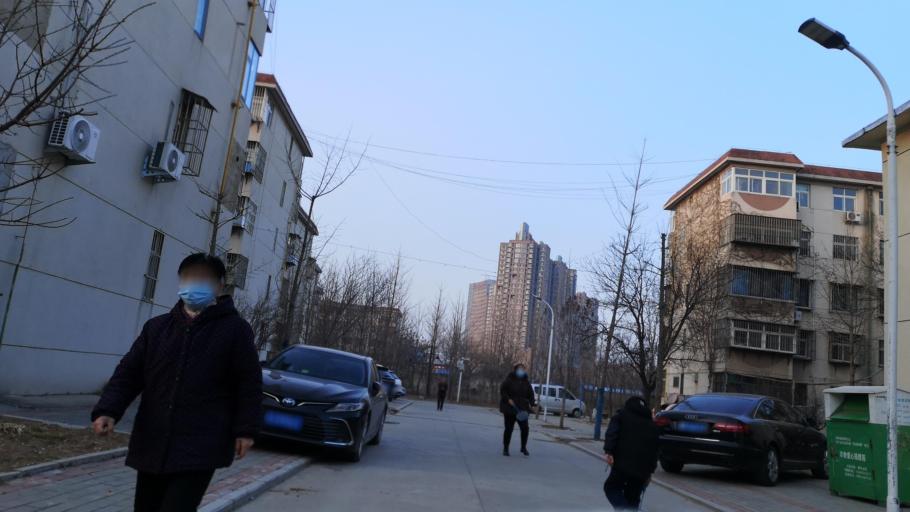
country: CN
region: Henan Sheng
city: Zhongyuanlu
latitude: 35.7688
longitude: 115.0803
